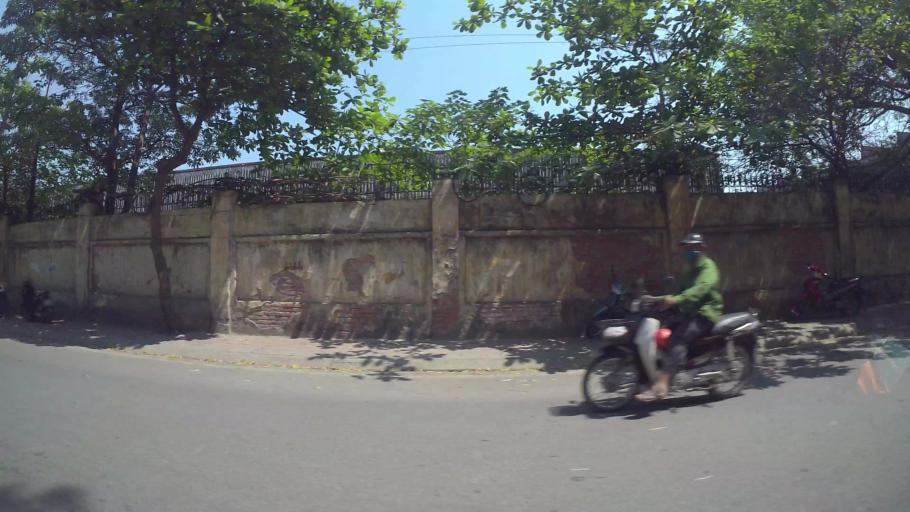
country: VN
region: Ha Noi
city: Hoan Kiem
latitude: 21.0499
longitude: 105.8791
